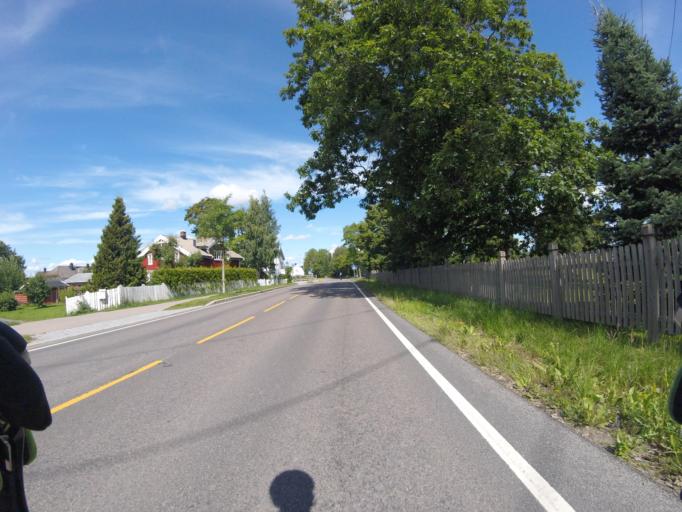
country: NO
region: Akershus
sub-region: Skedsmo
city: Lillestrom
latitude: 59.9452
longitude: 11.0195
